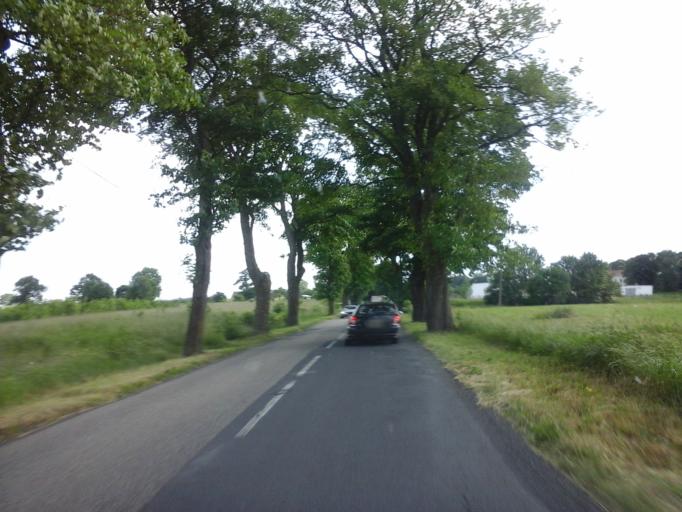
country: PL
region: West Pomeranian Voivodeship
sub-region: Powiat swidwinski
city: Swidwin
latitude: 53.7215
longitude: 15.7174
